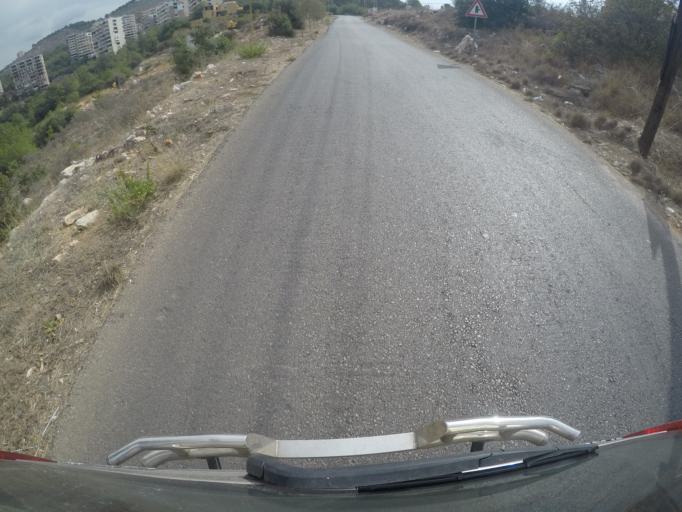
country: LB
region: Mont-Liban
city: Beit ed Dine
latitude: 33.7348
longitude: 35.4865
